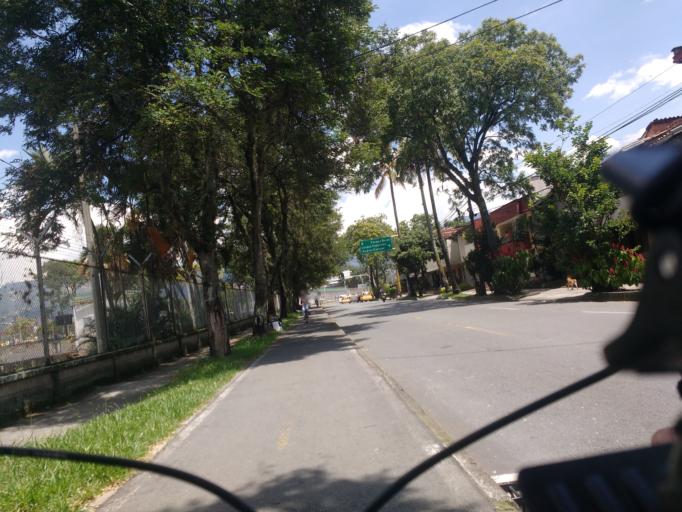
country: CO
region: Antioquia
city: Medellin
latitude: 6.2328
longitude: -75.5862
